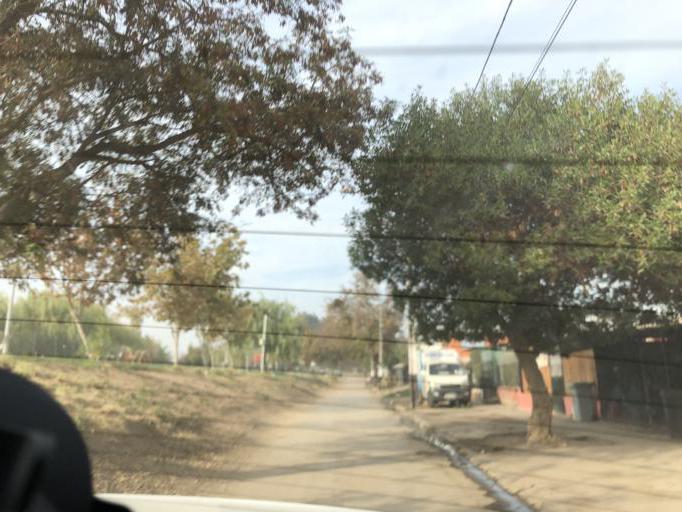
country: CL
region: Santiago Metropolitan
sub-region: Provincia de Cordillera
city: Puente Alto
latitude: -33.5619
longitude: -70.5532
